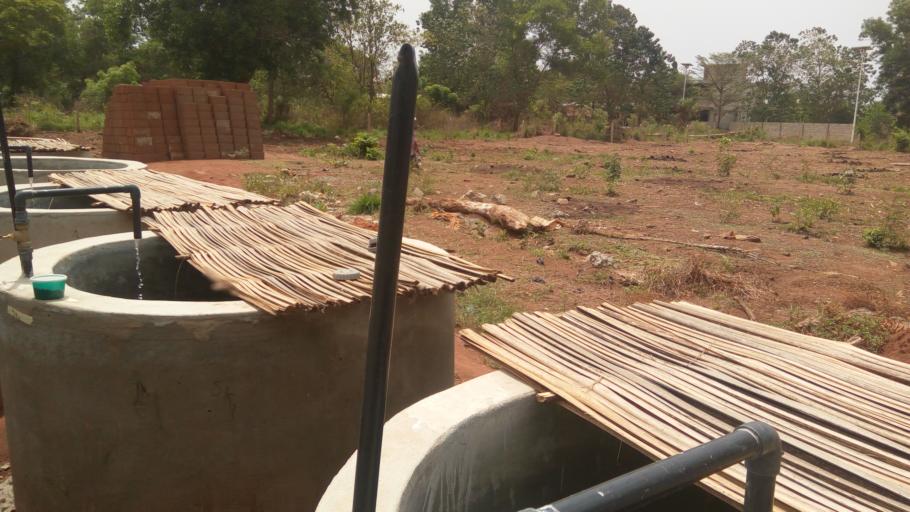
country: BJ
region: Atlantique
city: Abomey-Calavi
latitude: 6.4137
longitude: 2.3380
